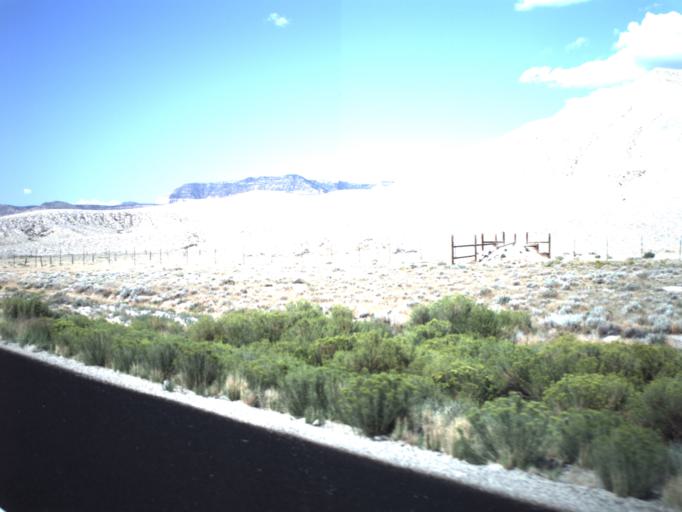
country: US
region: Utah
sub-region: Emery County
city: Ferron
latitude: 39.0035
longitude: -111.1577
